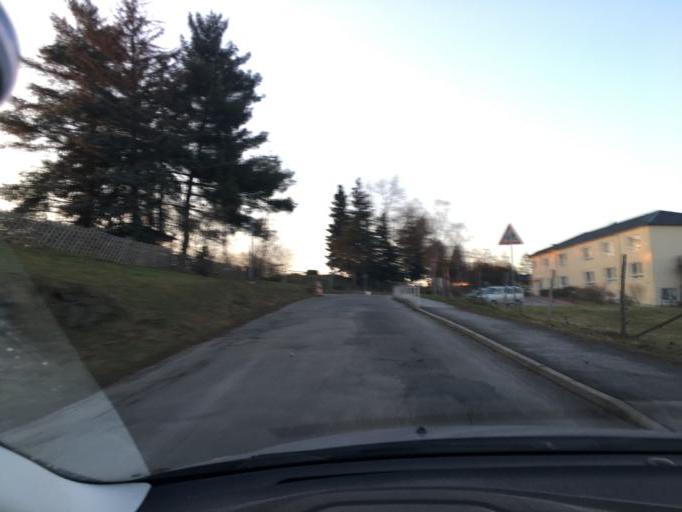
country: DE
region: Saxony
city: Lunzenau
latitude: 50.9633
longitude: 12.7522
